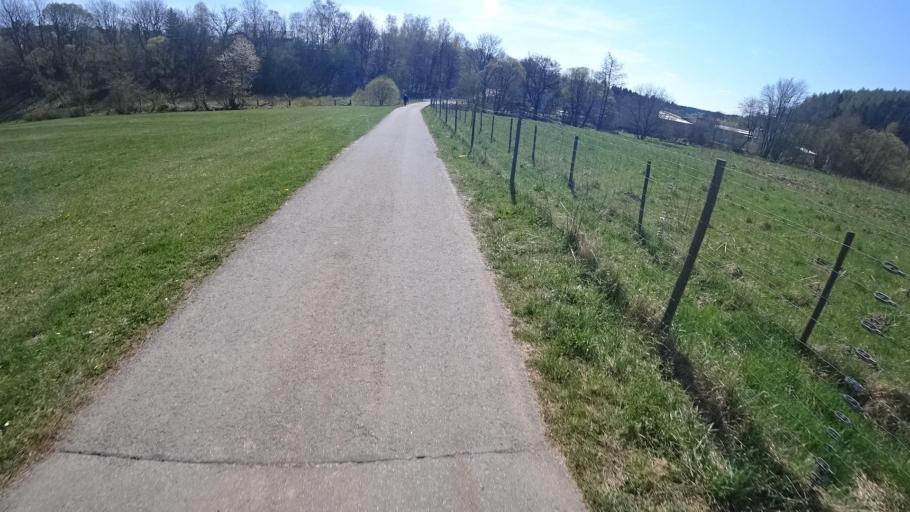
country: DE
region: Rheinland-Pfalz
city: Hermeskeil
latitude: 49.6551
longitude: 6.9288
